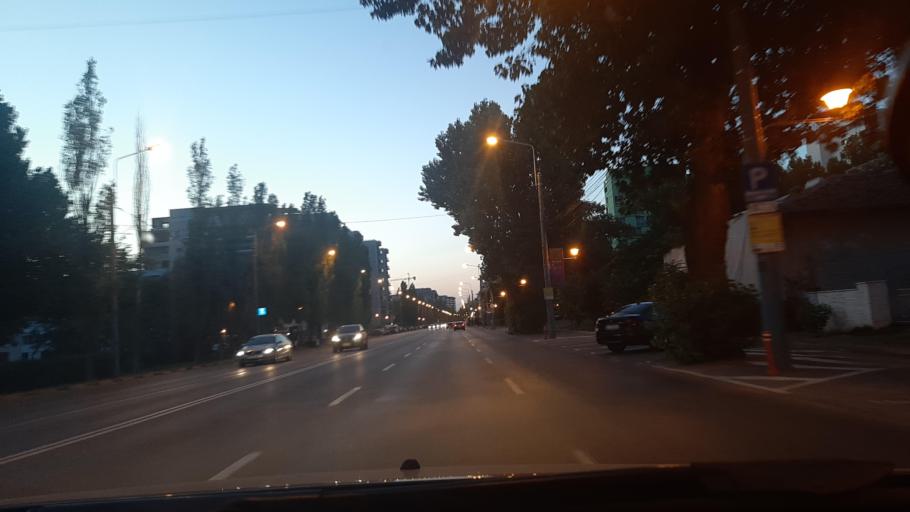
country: RO
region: Constanta
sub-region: Municipiul Constanta
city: Palazu Mare
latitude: 44.2375
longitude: 28.6222
